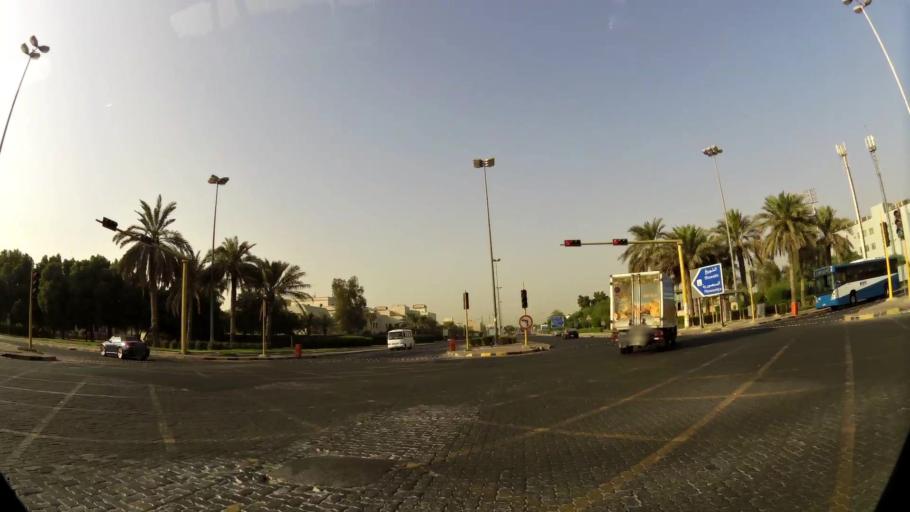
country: KW
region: Al Asimah
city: Ad Dasmah
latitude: 29.3571
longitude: 48.0033
